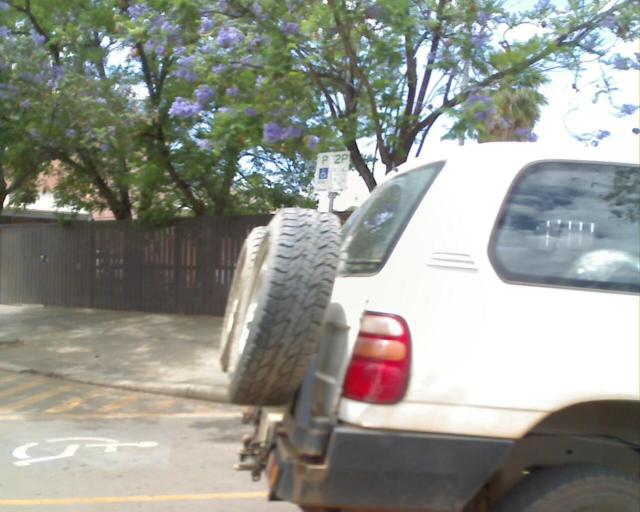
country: AU
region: Western Australia
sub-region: Kalgoorlie/Boulder
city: Boulder
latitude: -30.7819
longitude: 121.4881
